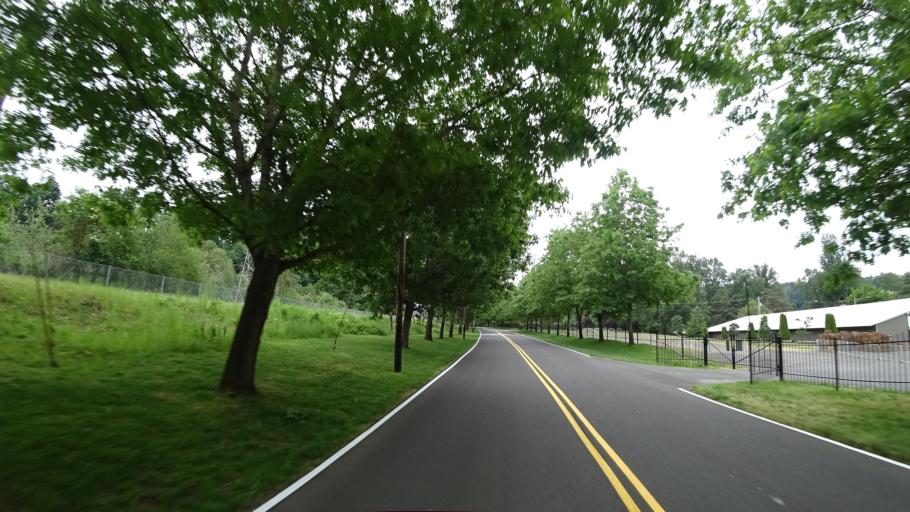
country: US
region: Oregon
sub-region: Clackamas County
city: Milwaukie
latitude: 45.4703
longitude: -122.6621
